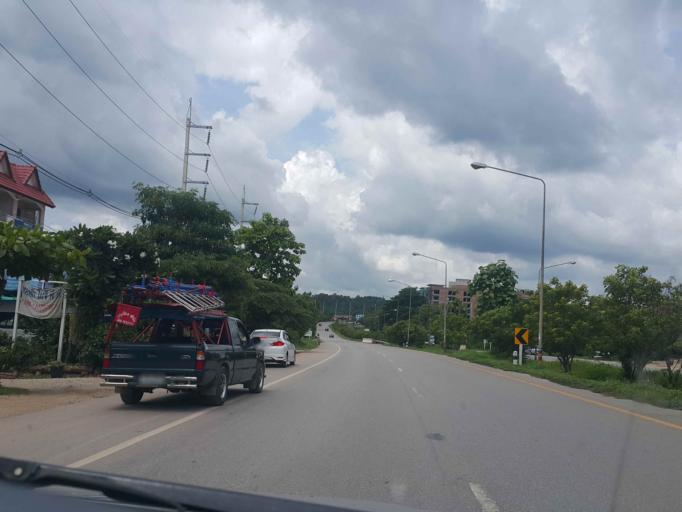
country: TH
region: Phayao
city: Dok Kham Tai
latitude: 19.0255
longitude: 99.9227
